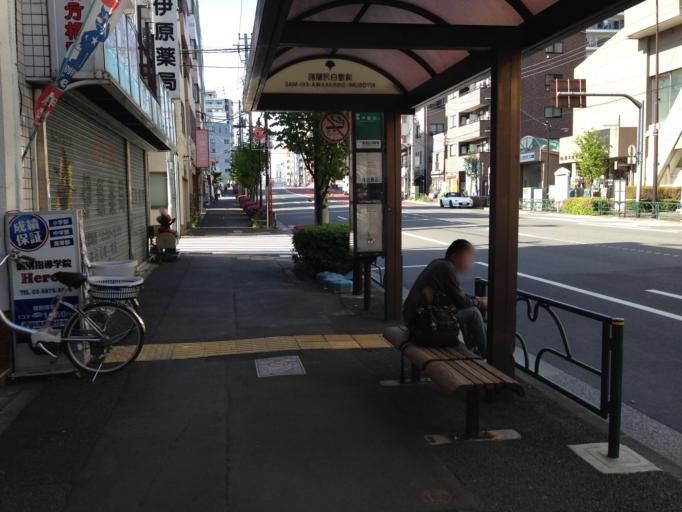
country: JP
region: Tokyo
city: Urayasu
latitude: 35.6823
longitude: 139.7988
